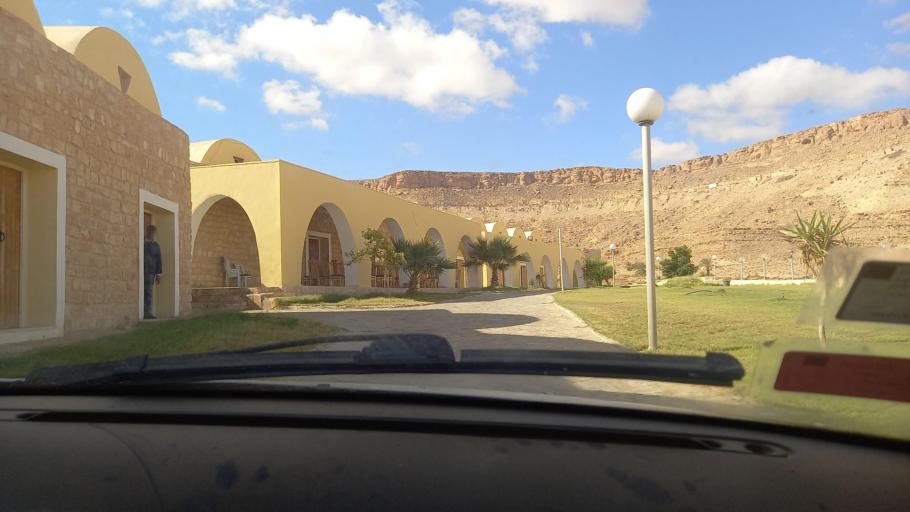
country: TN
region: Tataouine
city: Tataouine
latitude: 32.9830
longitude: 10.2594
